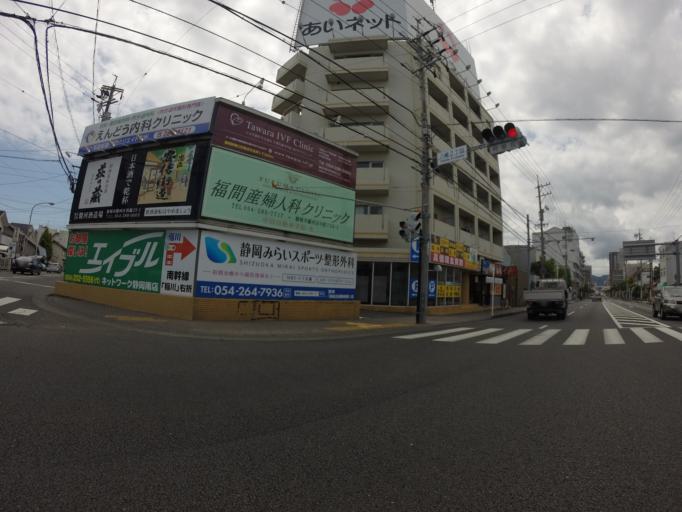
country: JP
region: Shizuoka
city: Shizuoka-shi
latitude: 34.9707
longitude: 138.3974
